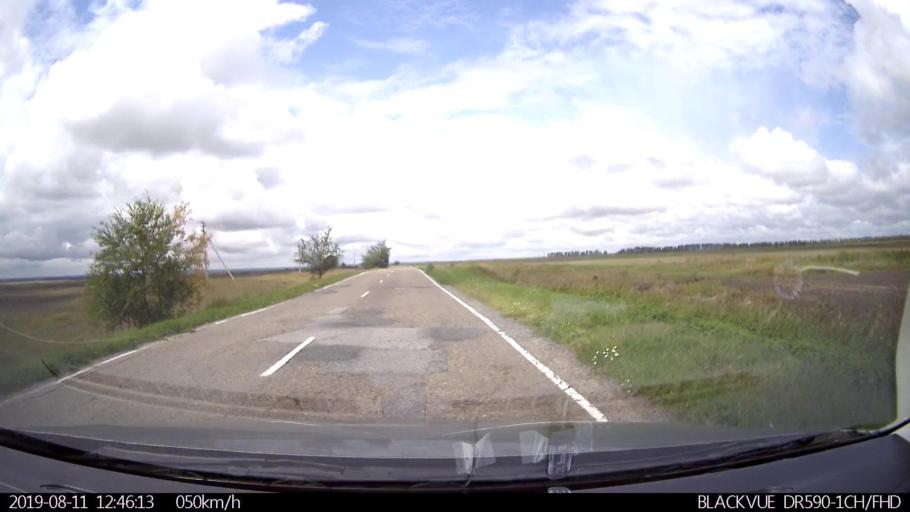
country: RU
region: Ulyanovsk
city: Ignatovka
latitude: 53.8632
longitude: 47.7209
